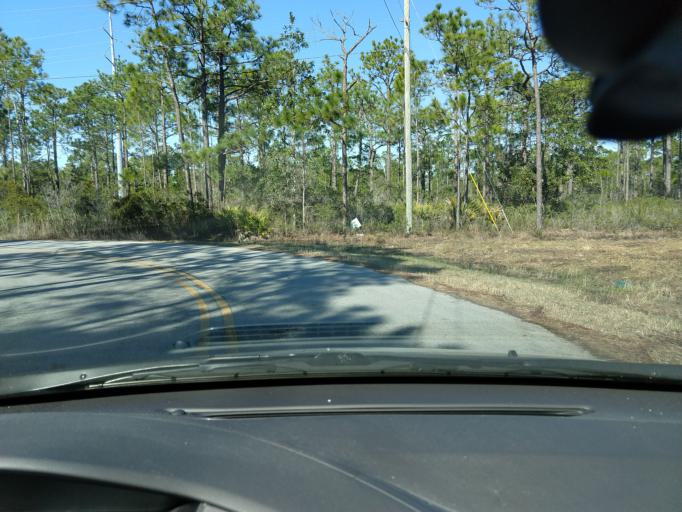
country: US
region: Florida
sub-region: Walton County
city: Miramar Beach
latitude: 30.3792
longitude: -86.3022
